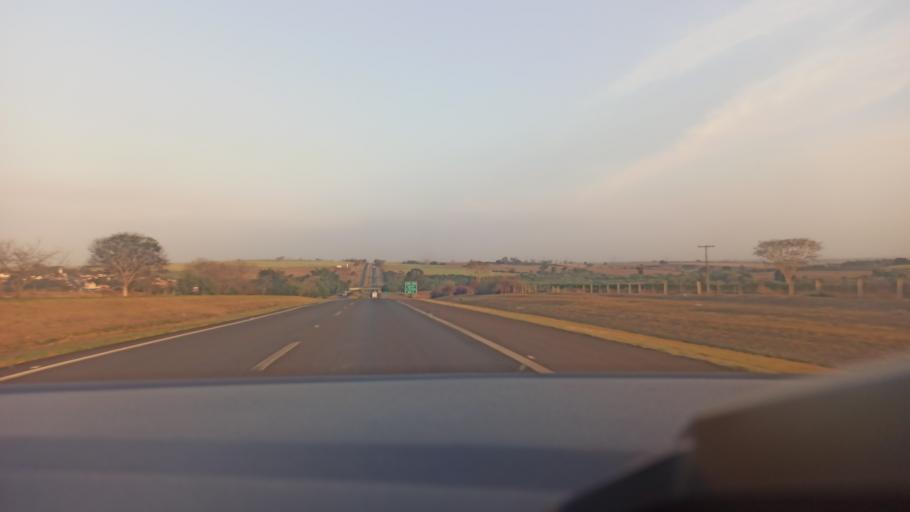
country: BR
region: Sao Paulo
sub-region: Santa Adelia
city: Santa Adelia
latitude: -21.3664
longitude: -48.7562
